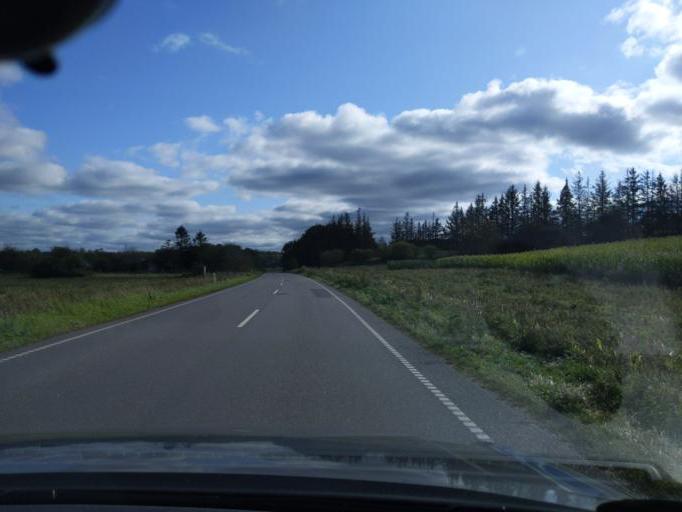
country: DK
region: North Denmark
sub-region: Mariagerfjord Kommune
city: Hobro
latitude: 56.5580
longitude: 9.7249
